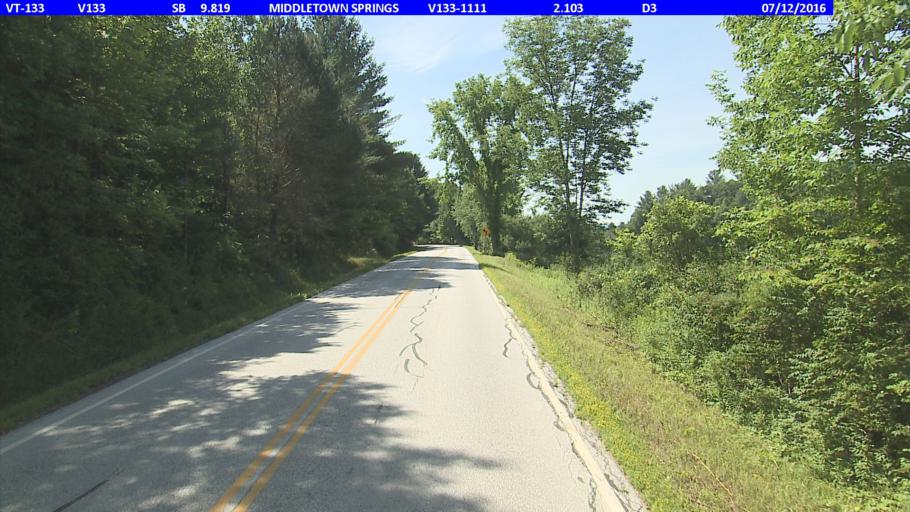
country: US
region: Vermont
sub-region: Rutland County
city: Poultney
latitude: 43.4650
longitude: -73.1133
